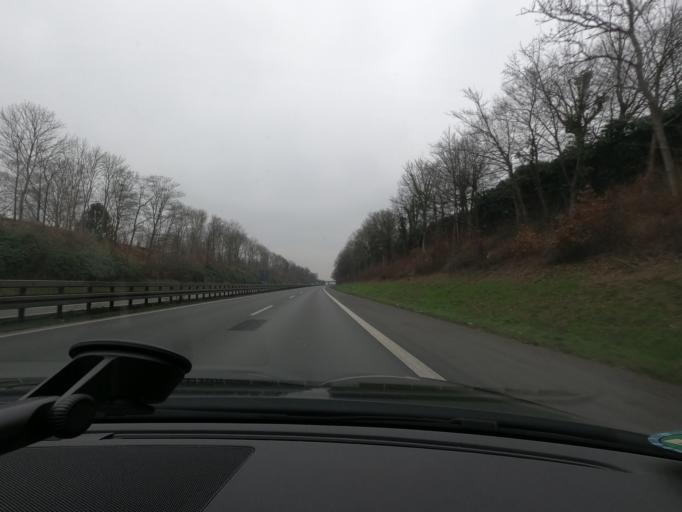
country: DE
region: North Rhine-Westphalia
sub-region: Regierungsbezirk Dusseldorf
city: Monchengladbach
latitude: 51.1803
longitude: 6.3987
